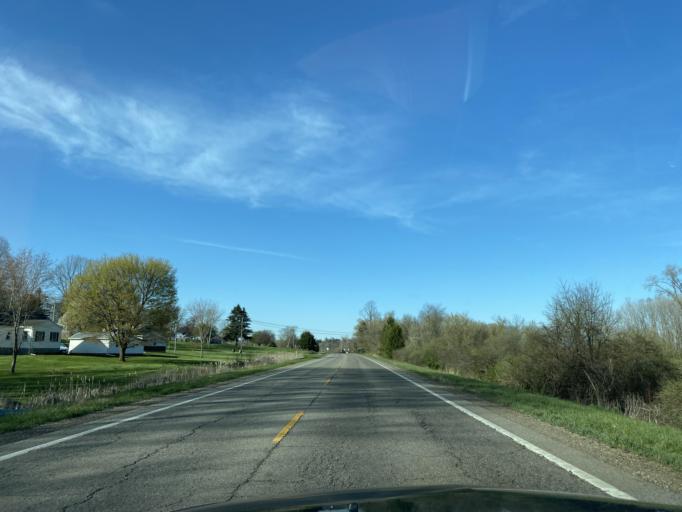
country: US
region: Ohio
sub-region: Wayne County
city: Shreve
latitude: 40.7198
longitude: -82.0008
